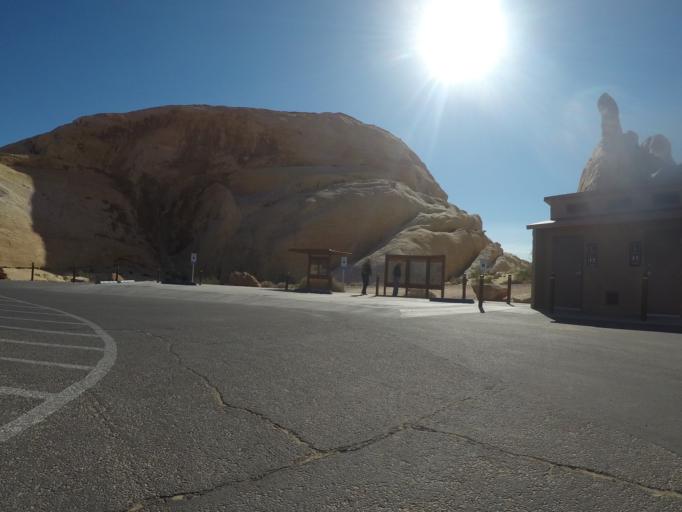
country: US
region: Nevada
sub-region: Clark County
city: Moapa Valley
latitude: 36.4859
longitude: -114.5330
